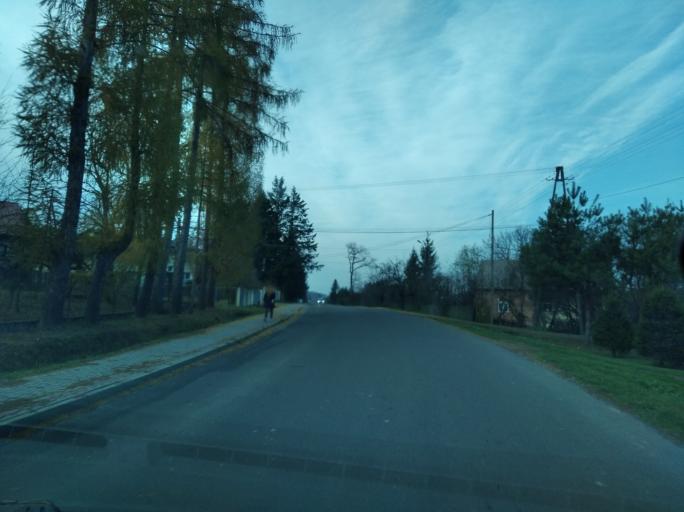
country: PL
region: Subcarpathian Voivodeship
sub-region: Powiat ropczycko-sedziszowski
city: Iwierzyce
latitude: 50.0302
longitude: 21.7550
